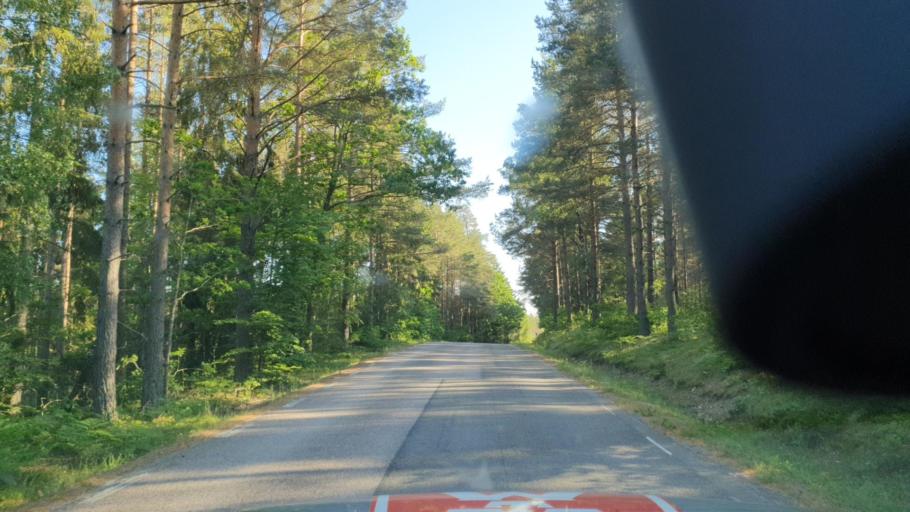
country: SE
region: Kalmar
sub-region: Torsas Kommun
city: Torsas
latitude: 56.4926
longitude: 16.1022
